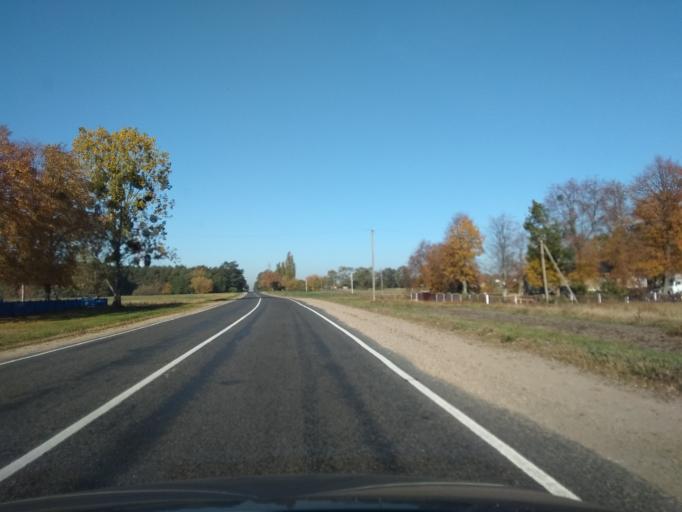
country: BY
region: Brest
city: Malaryta
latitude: 51.9271
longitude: 24.0698
